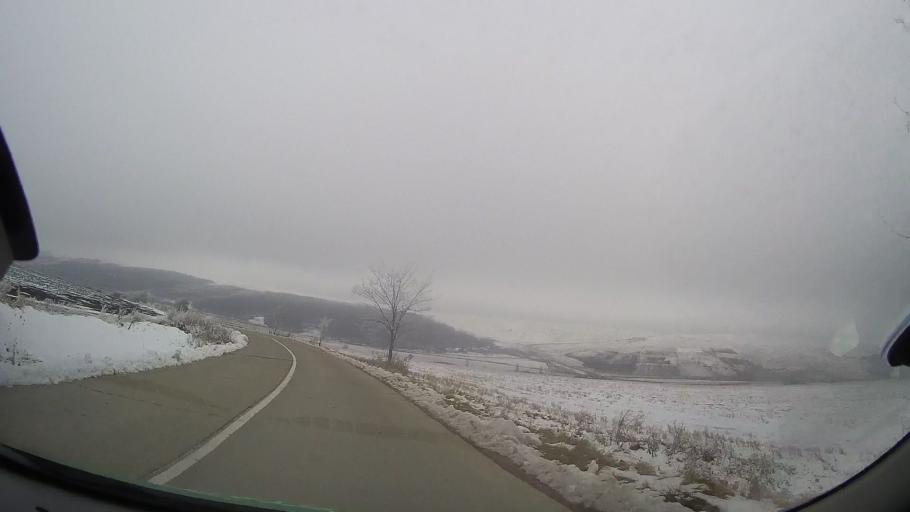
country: RO
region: Vaslui
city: Coroiesti
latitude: 46.2104
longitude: 27.4849
